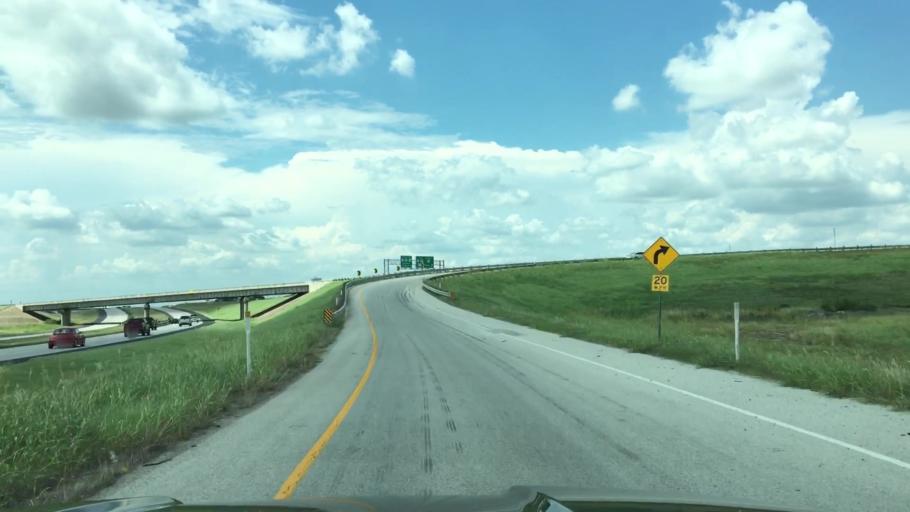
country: US
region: Texas
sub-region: Wise County
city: Rhome
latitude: 33.0440
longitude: -97.4614
